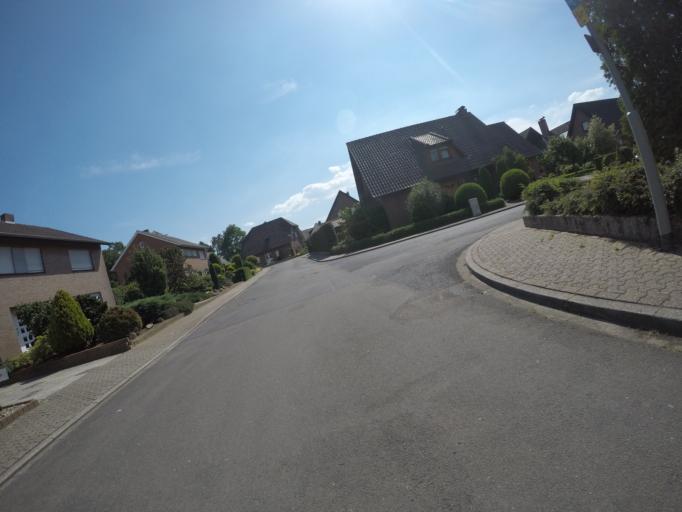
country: DE
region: North Rhine-Westphalia
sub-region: Regierungsbezirk Munster
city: Isselburg
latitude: 51.8507
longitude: 6.4249
